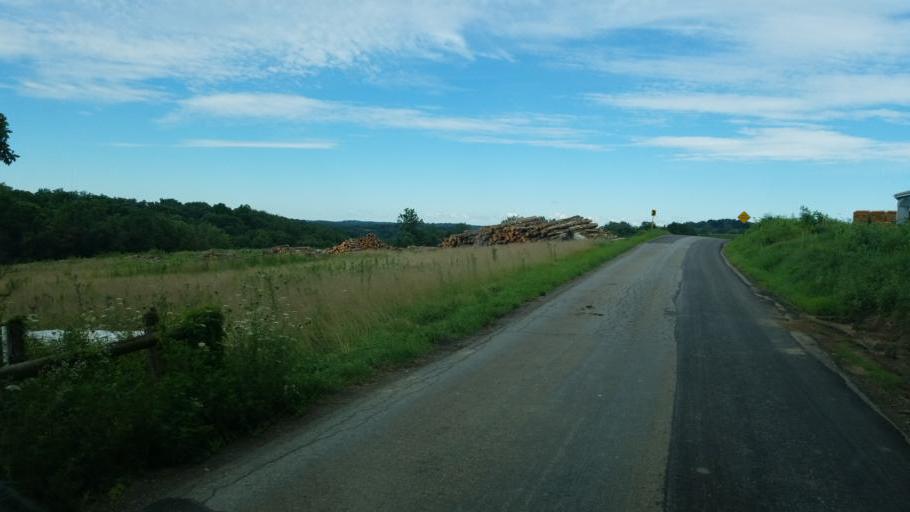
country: US
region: Ohio
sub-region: Holmes County
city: Millersburg
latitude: 40.4952
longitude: -81.8286
